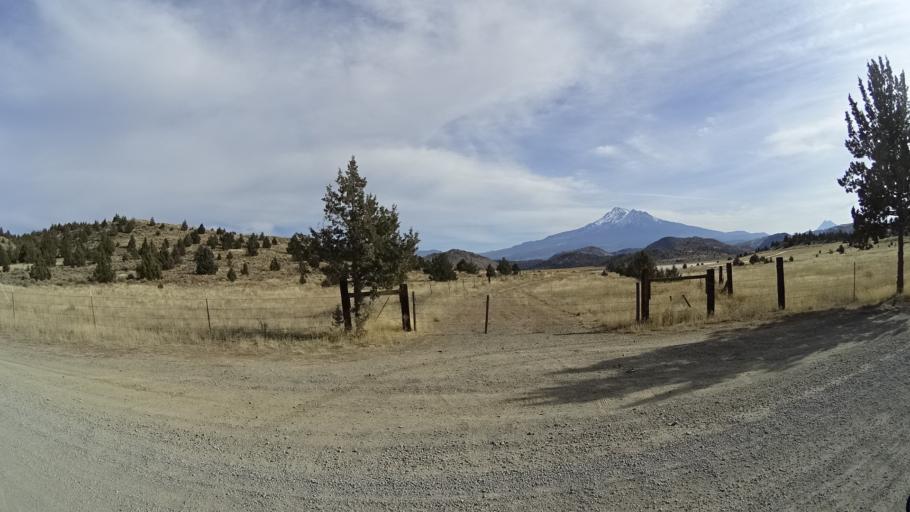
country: US
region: California
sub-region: Siskiyou County
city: Weed
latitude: 41.5634
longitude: -122.4681
